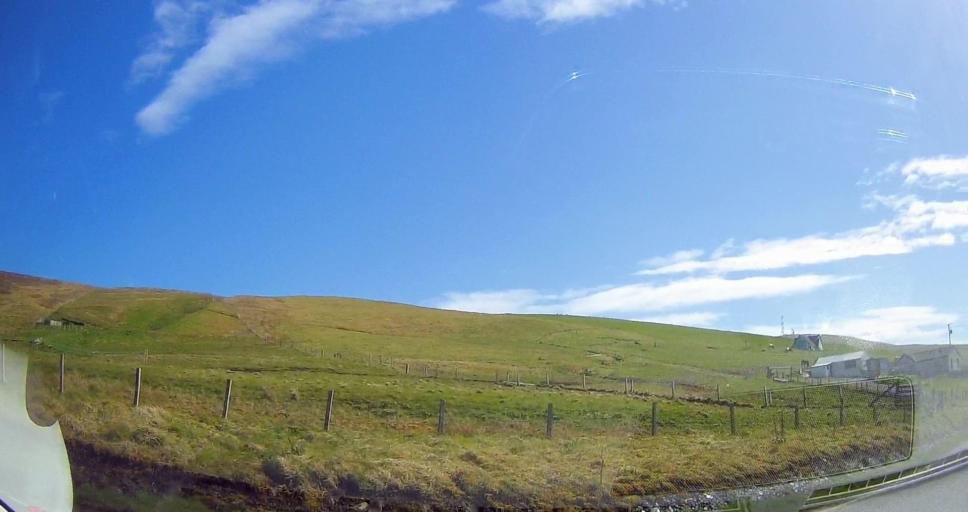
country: GB
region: Scotland
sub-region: Shetland Islands
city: Sandwick
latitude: 59.9723
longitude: -1.3157
